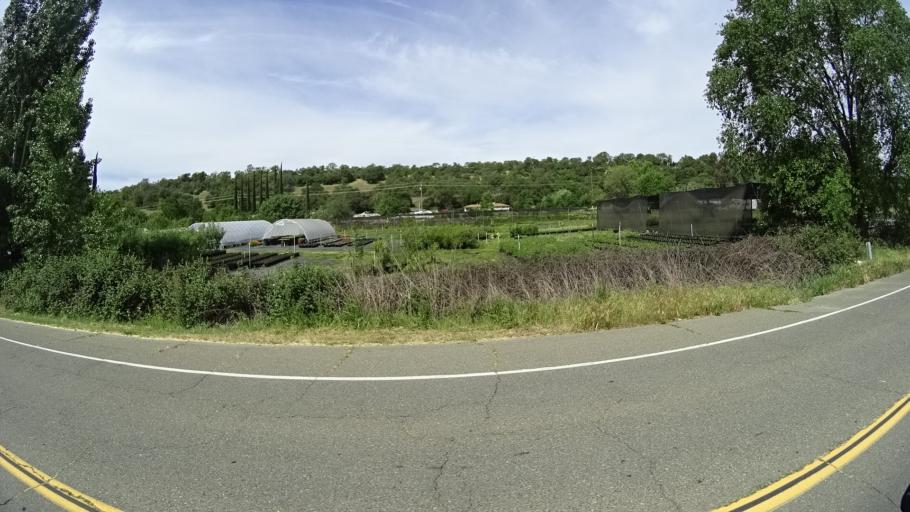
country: US
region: California
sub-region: Placer County
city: Loomis
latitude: 38.8288
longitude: -121.2175
